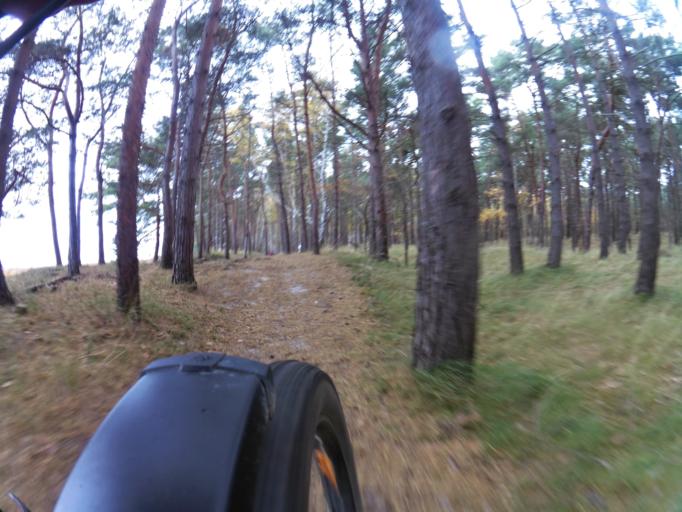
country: PL
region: Pomeranian Voivodeship
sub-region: Powiat pucki
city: Jastarnia
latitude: 54.6893
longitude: 18.6987
